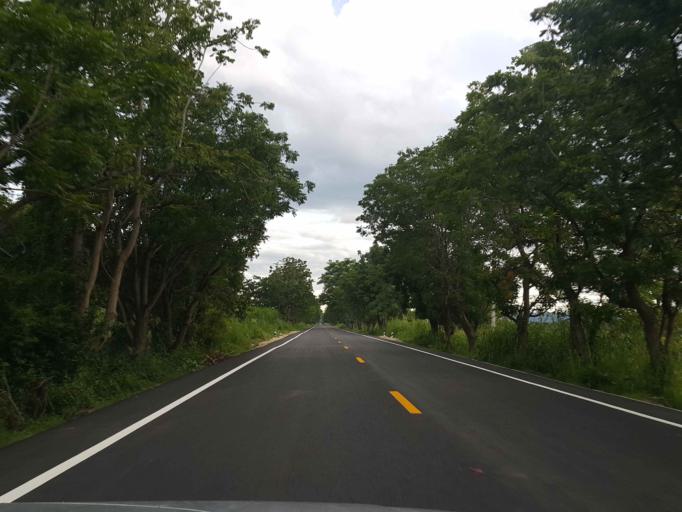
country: TH
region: Sukhothai
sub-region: Amphoe Si Satchanalai
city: Si Satchanalai
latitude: 17.4865
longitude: 99.7460
